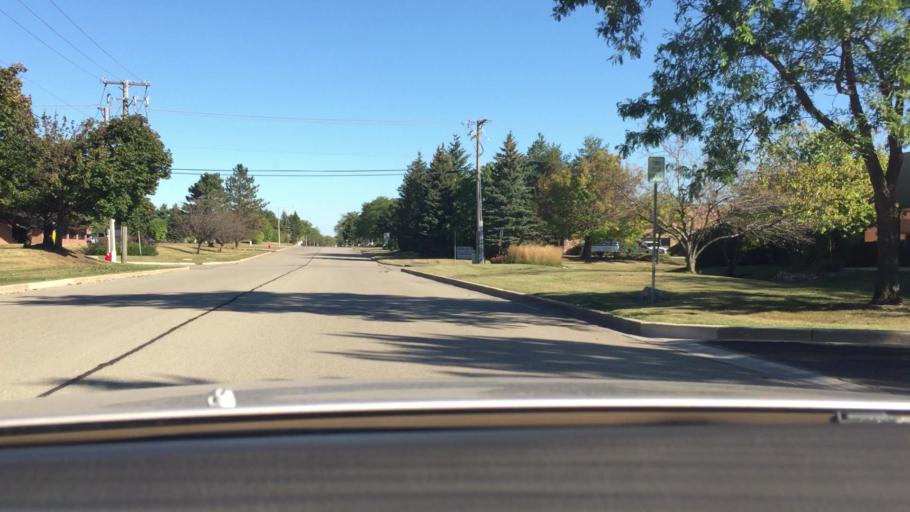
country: US
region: Illinois
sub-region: Lake County
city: Forest Lake
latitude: 42.2041
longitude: -88.0676
